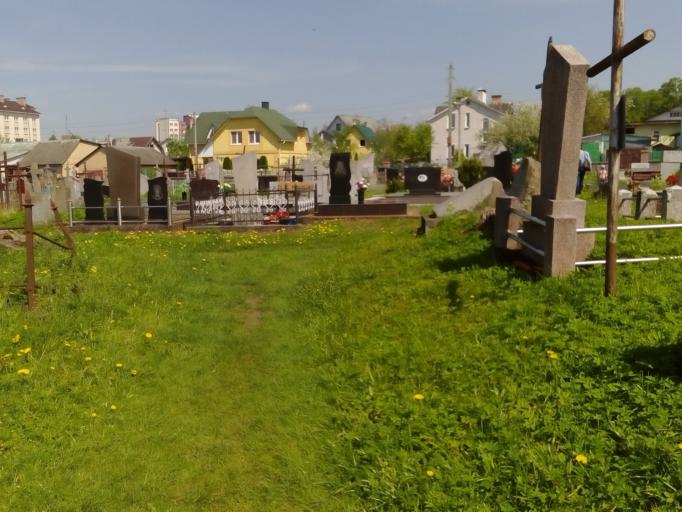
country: BY
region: Grodnenskaya
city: Hrodna
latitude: 53.6690
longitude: 23.8441
